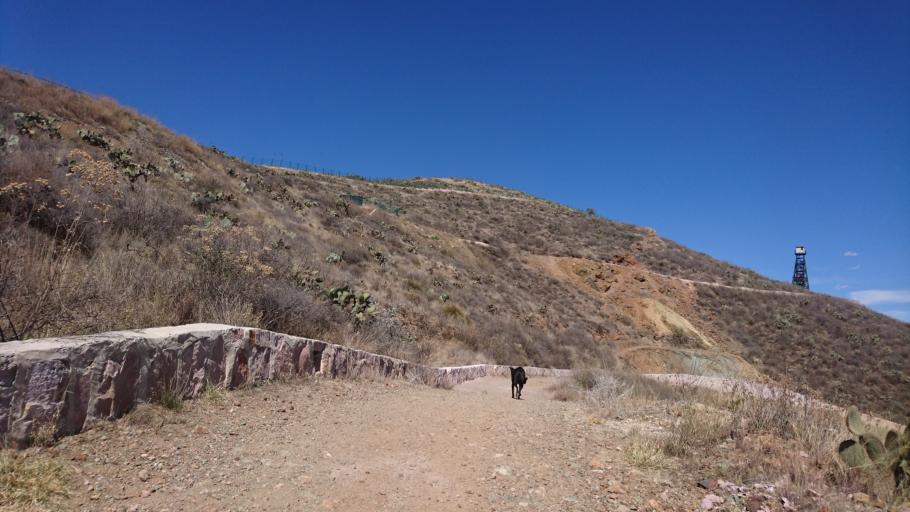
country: MX
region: Zacatecas
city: Zacatecas
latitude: 22.7779
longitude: -102.5480
